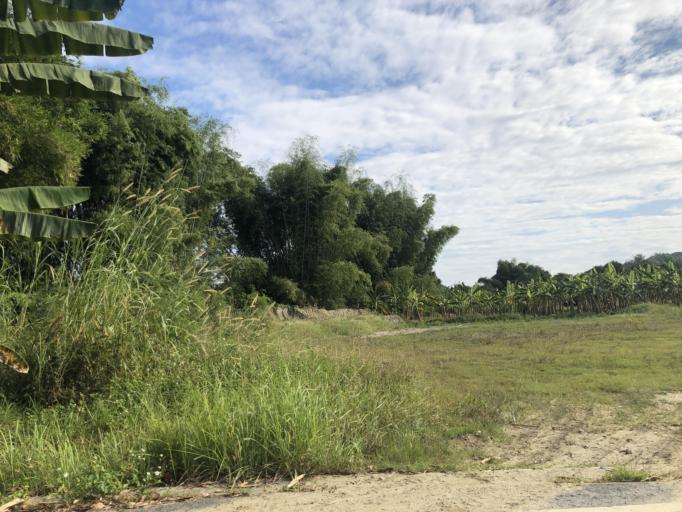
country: TW
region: Taiwan
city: Yujing
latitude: 23.0488
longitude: 120.4014
